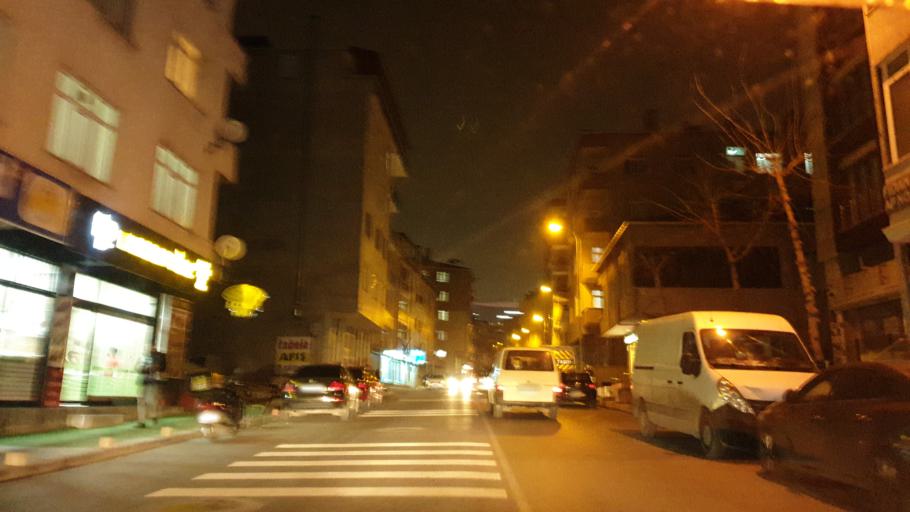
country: TR
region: Istanbul
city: Pendik
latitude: 40.8763
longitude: 29.2543
